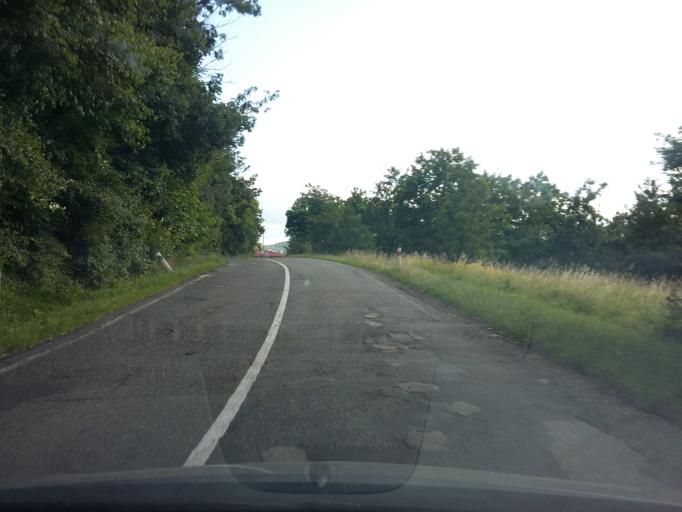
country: SK
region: Trnavsky
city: Smolenice
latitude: 48.5174
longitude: 17.3067
